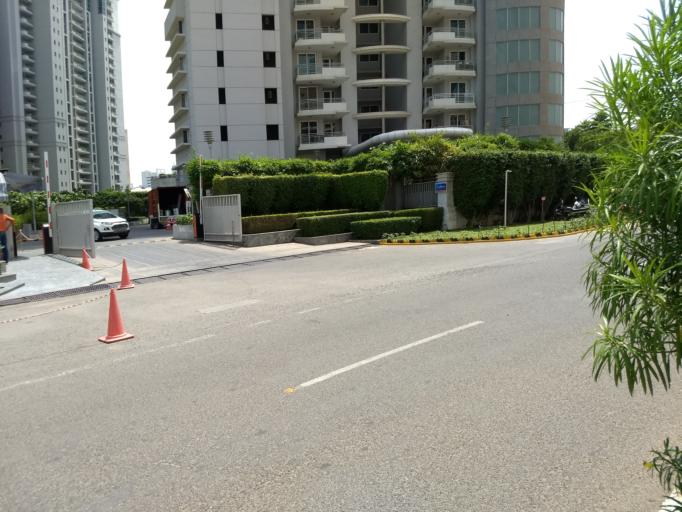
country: IN
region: Haryana
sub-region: Gurgaon
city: Gurgaon
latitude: 28.4498
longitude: 77.1014
